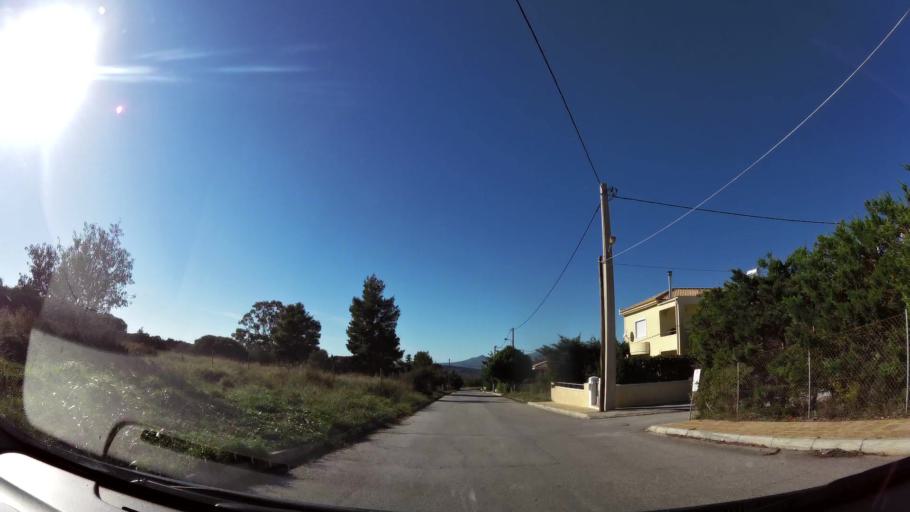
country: GR
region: Attica
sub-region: Nomarchia Anatolikis Attikis
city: Kalyvia Thorikou
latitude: 37.8329
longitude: 23.9282
